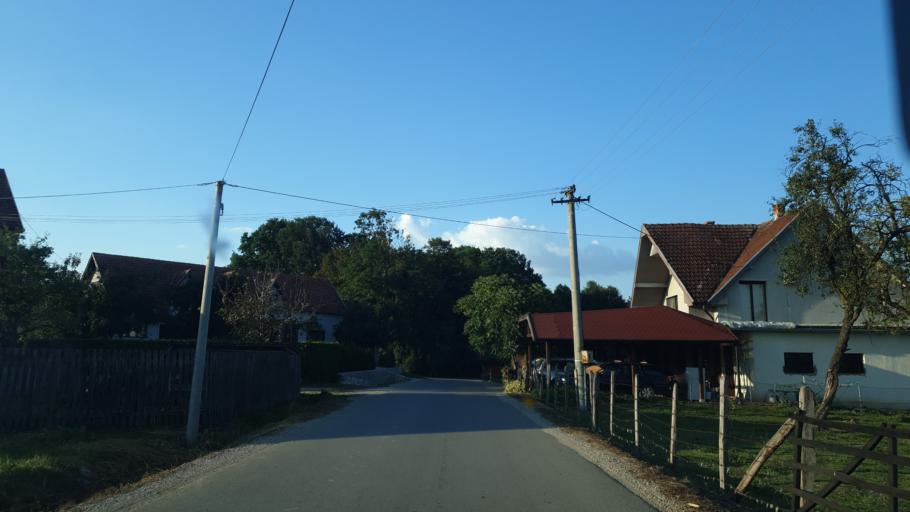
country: RS
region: Central Serbia
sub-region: Zlatiborski Okrug
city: Pozega
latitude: 43.8712
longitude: 19.9913
